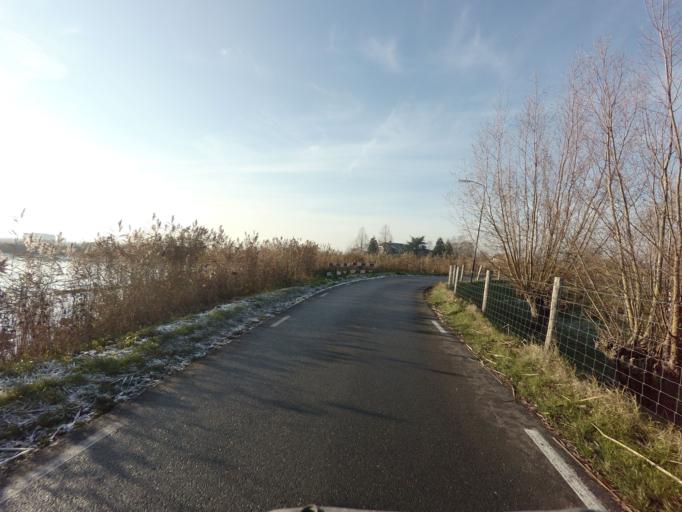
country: NL
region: Utrecht
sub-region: Gemeente De Ronde Venen
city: Mijdrecht
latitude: 52.1908
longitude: 4.8284
